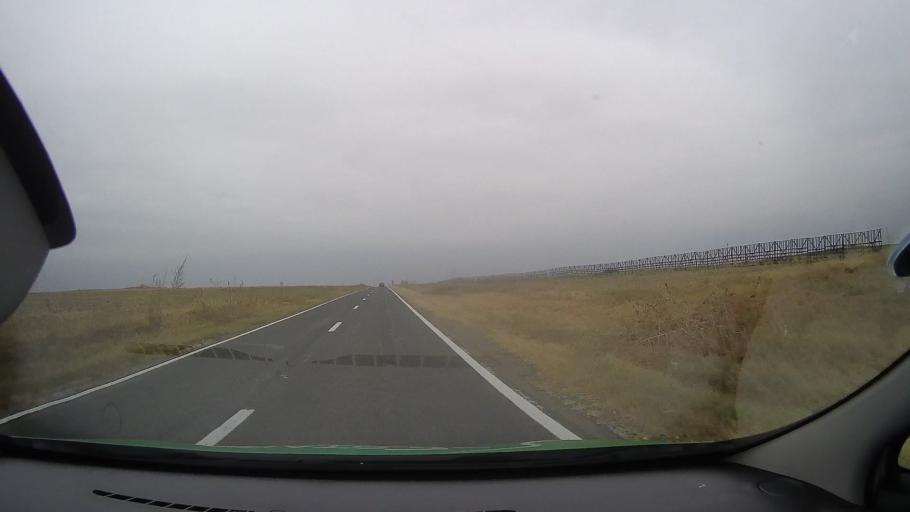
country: RO
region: Constanta
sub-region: Comuna Ciobanu
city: Ciobanu
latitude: 44.7027
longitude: 28.0267
